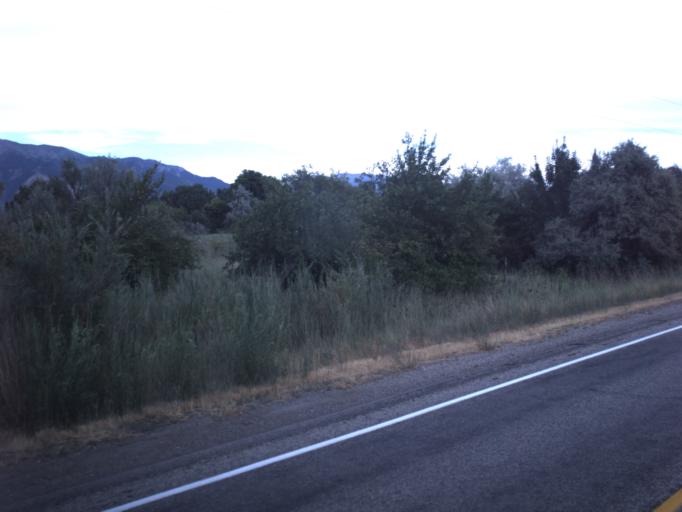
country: US
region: Utah
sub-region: Weber County
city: Marriott-Slaterville
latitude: 41.2578
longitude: -112.0252
